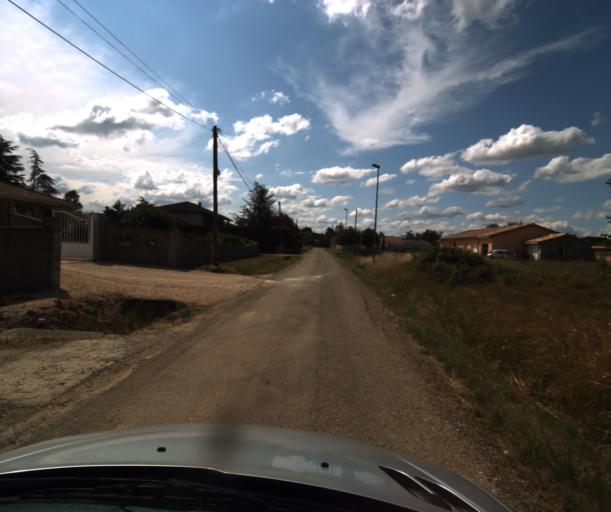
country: FR
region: Midi-Pyrenees
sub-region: Departement du Tarn-et-Garonne
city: Finhan
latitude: 43.9217
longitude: 1.2761
